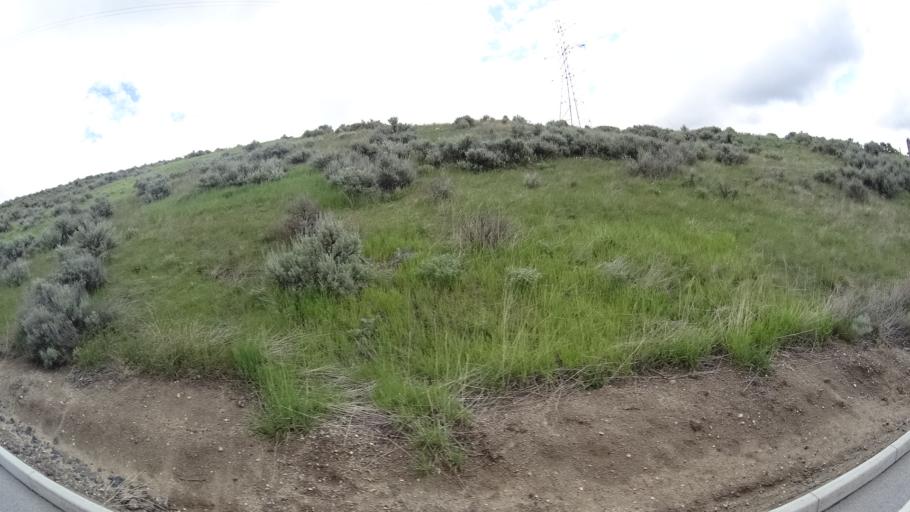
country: US
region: Idaho
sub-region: Ada County
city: Boise
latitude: 43.6986
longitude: -116.1687
